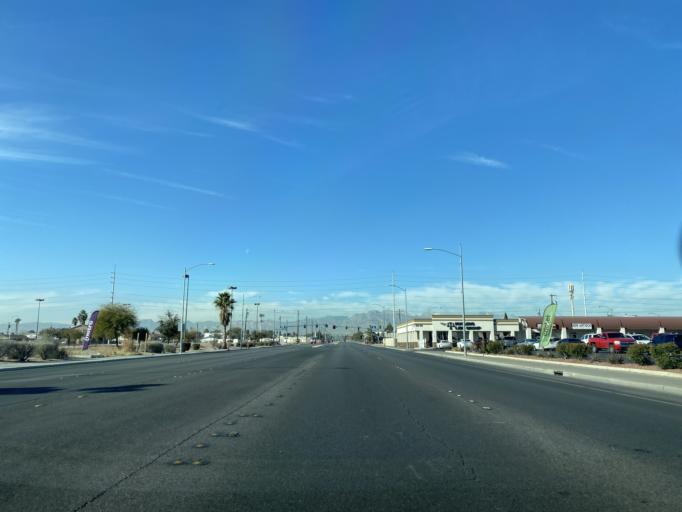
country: US
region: Nevada
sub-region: Clark County
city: Las Vegas
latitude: 36.1885
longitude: -115.1542
